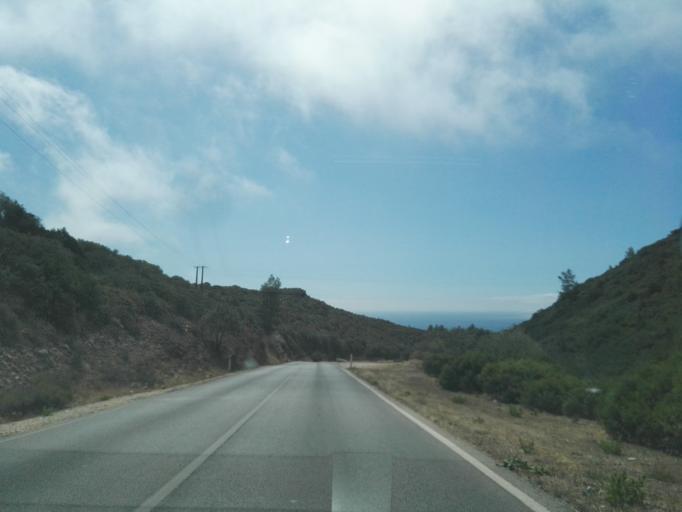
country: PT
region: Setubal
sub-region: Sesimbra
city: Sesimbra
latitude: 38.4442
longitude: -9.0864
